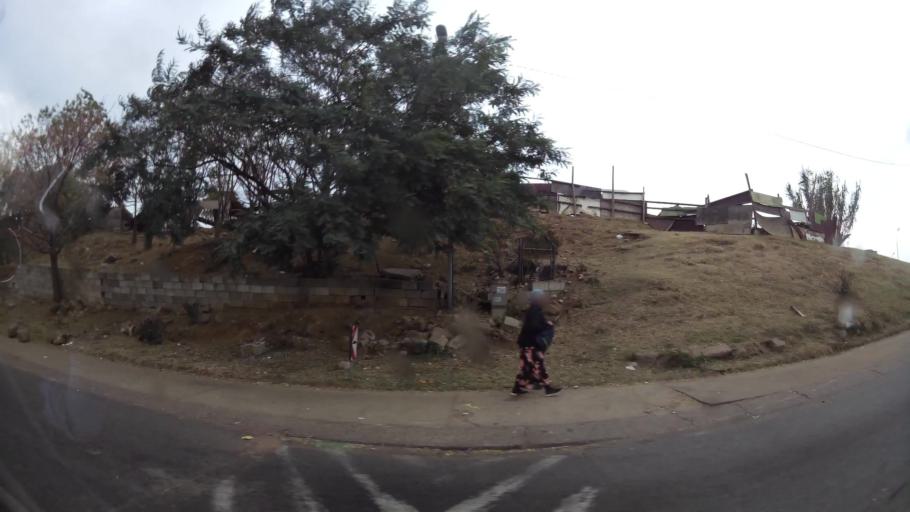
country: ZA
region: Gauteng
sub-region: City of Tshwane Metropolitan Municipality
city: Pretoria
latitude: -25.7168
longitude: 28.3557
